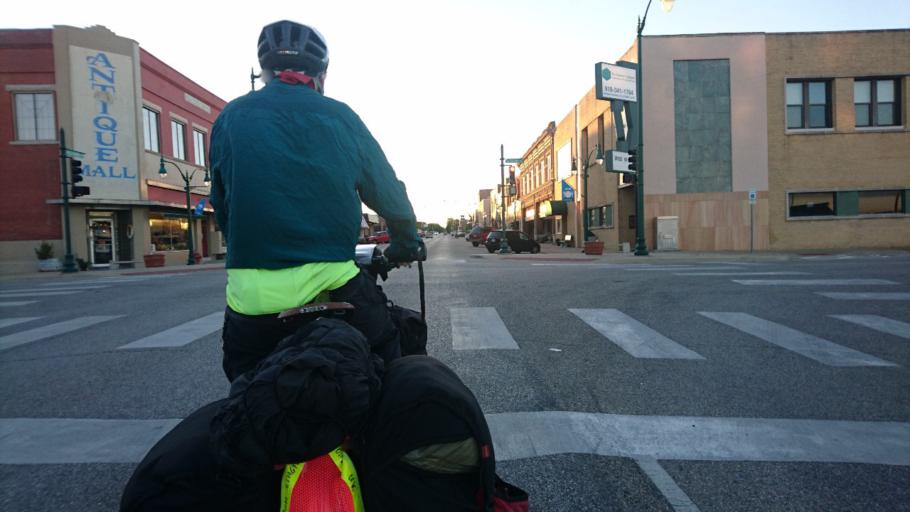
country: US
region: Oklahoma
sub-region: Rogers County
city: Claremore
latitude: 36.3122
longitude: -95.6151
